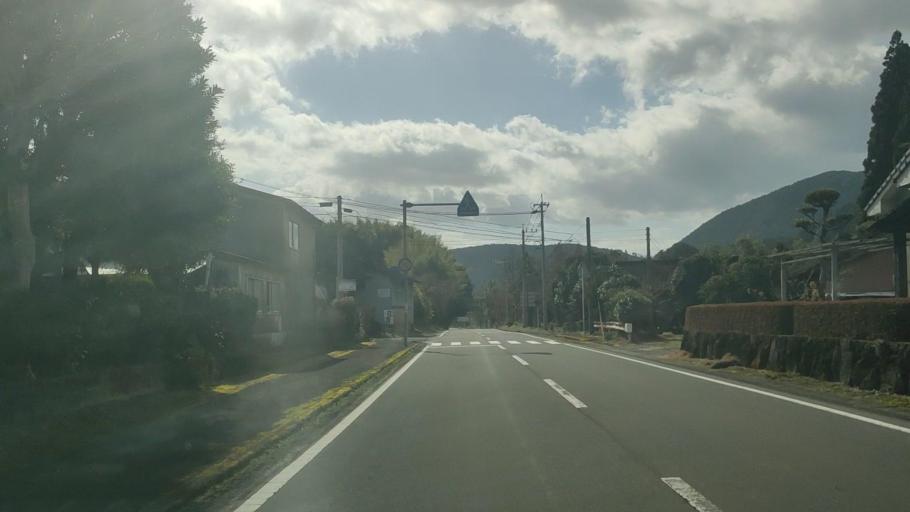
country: JP
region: Kagoshima
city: Okuchi-shinohara
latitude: 31.9885
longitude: 130.7442
